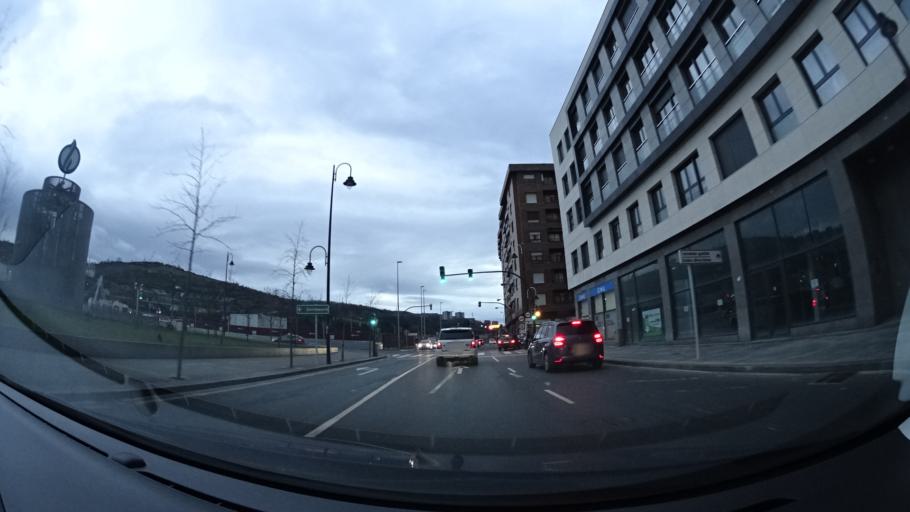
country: ES
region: Basque Country
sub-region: Bizkaia
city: Bilbao
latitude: 43.2683
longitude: -2.9534
